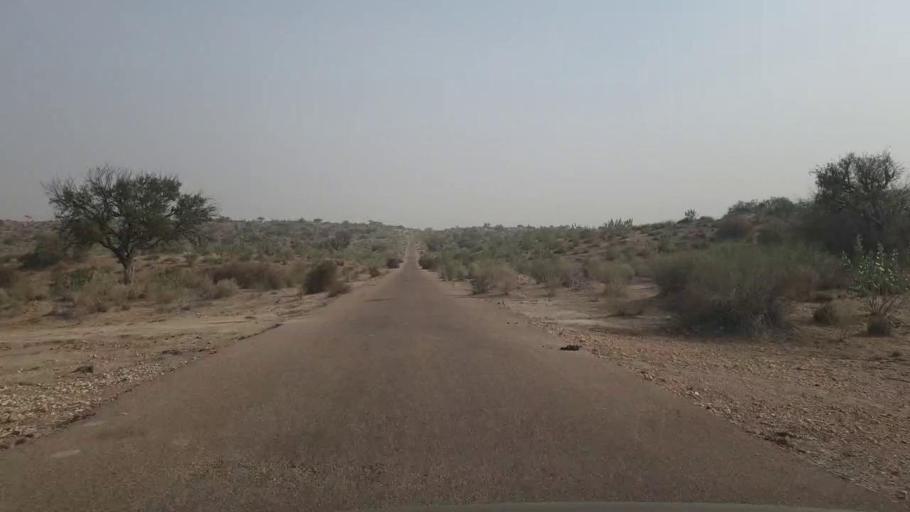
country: PK
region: Sindh
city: Chor
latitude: 25.4888
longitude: 69.9725
